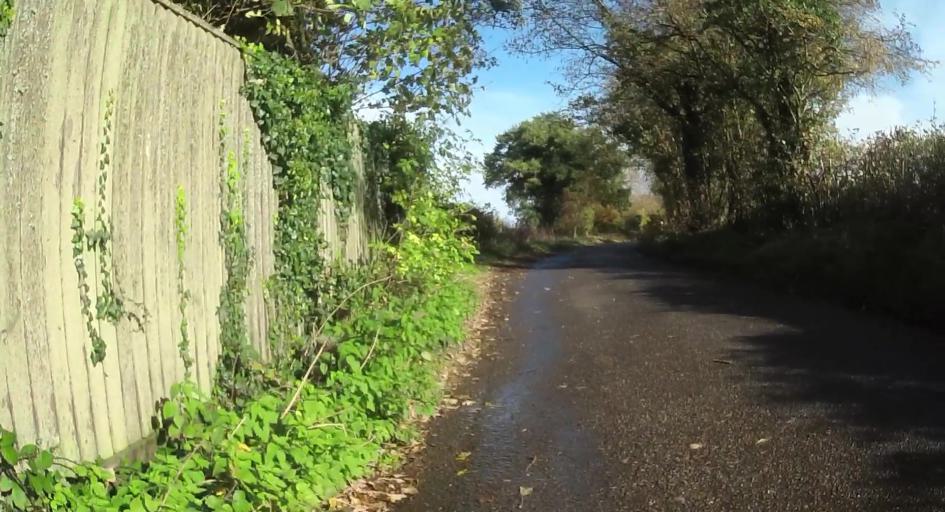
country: GB
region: England
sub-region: Hampshire
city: Four Marks
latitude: 51.1445
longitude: -1.0933
